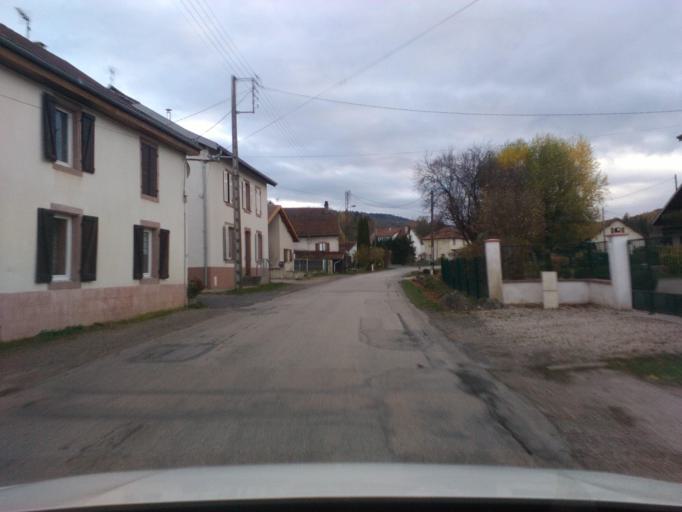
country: FR
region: Lorraine
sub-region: Departement des Vosges
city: Ban-de-Laveline
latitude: 48.2421
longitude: 7.0658
